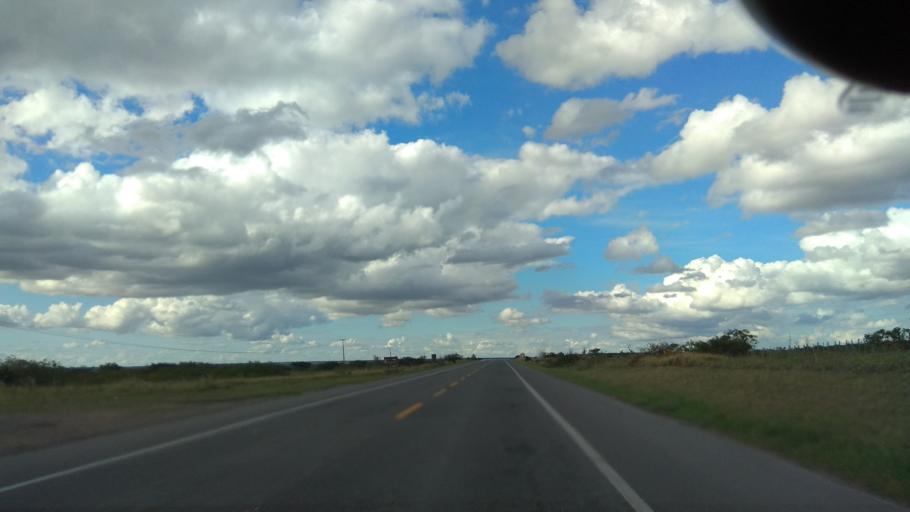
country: BR
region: Bahia
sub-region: Castro Alves
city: Castro Alves
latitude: -12.6076
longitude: -39.5582
